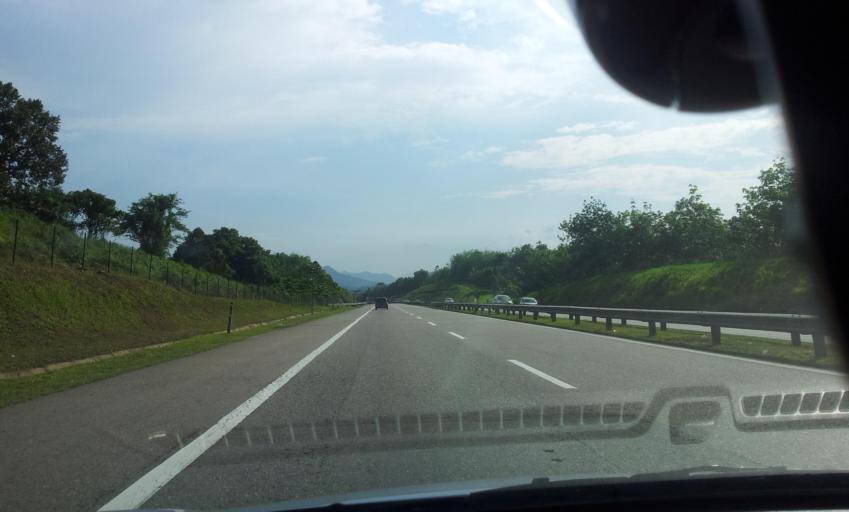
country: MY
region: Pahang
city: Bentong Town
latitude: 3.4697
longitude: 102.0550
